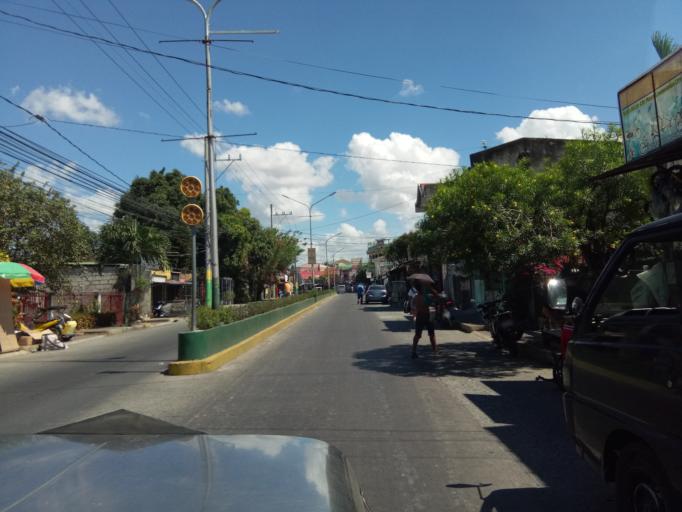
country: PH
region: Calabarzon
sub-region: Province of Cavite
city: Dasmarinas
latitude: 14.3413
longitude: 120.9482
